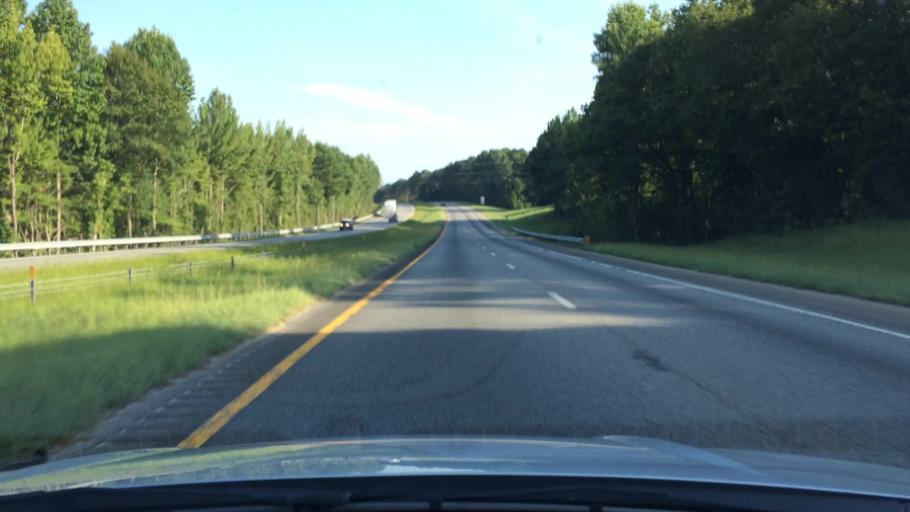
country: US
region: South Carolina
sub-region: Spartanburg County
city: Woodruff
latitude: 34.7417
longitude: -81.9544
